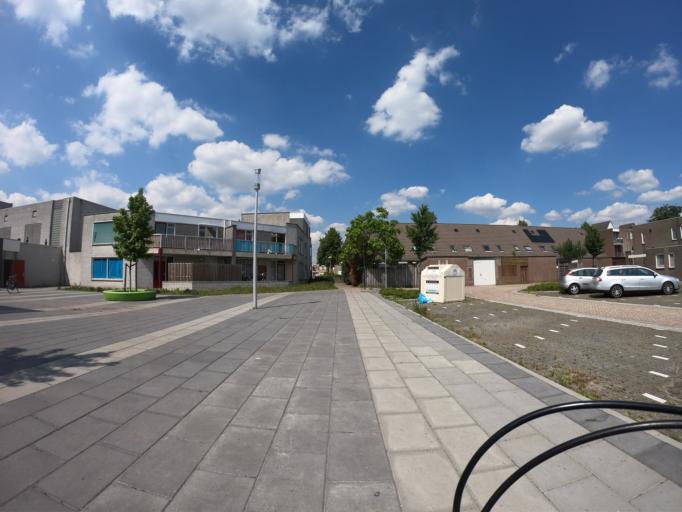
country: NL
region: North Brabant
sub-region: Gemeente Uden
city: Uden
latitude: 51.6520
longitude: 5.6167
